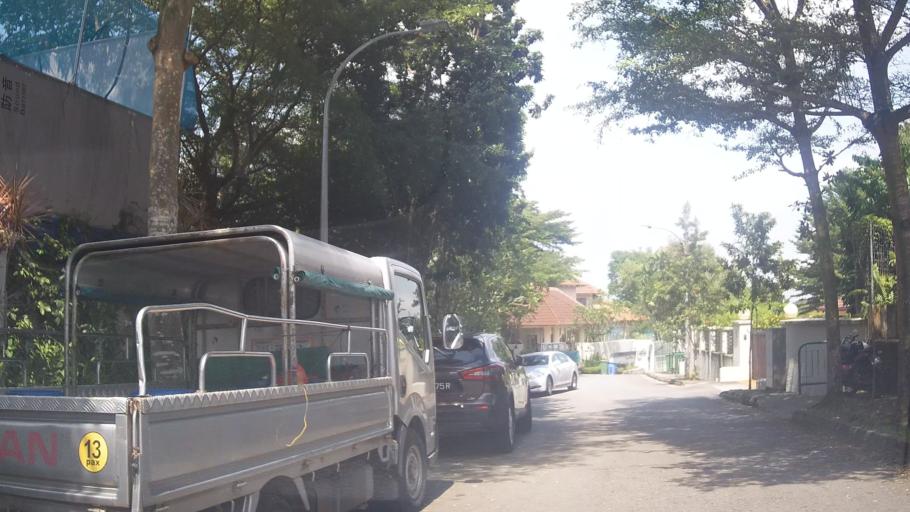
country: SG
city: Singapore
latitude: 1.3191
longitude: 103.8030
